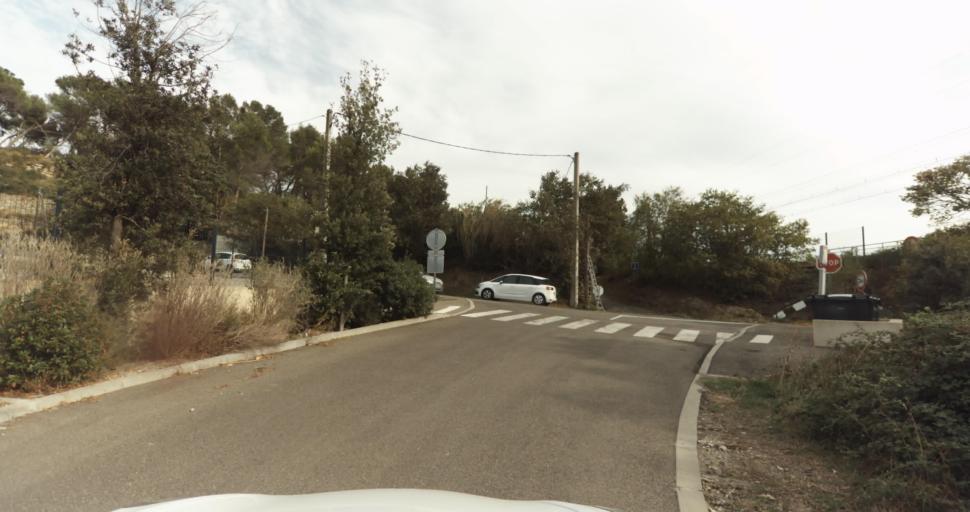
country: FR
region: Provence-Alpes-Cote d'Azur
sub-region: Departement des Bouches-du-Rhone
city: Miramas
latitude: 43.5758
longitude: 5.0224
